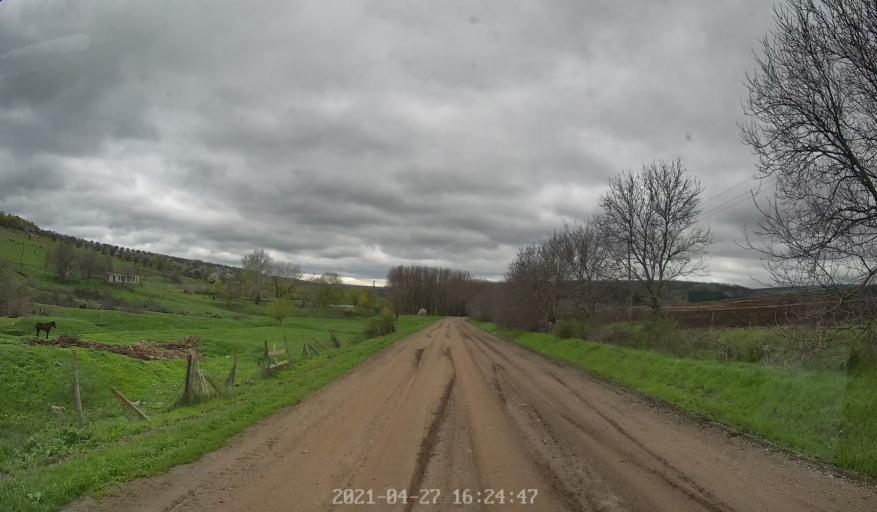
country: MD
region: Chisinau
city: Singera
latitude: 46.9894
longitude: 29.0212
